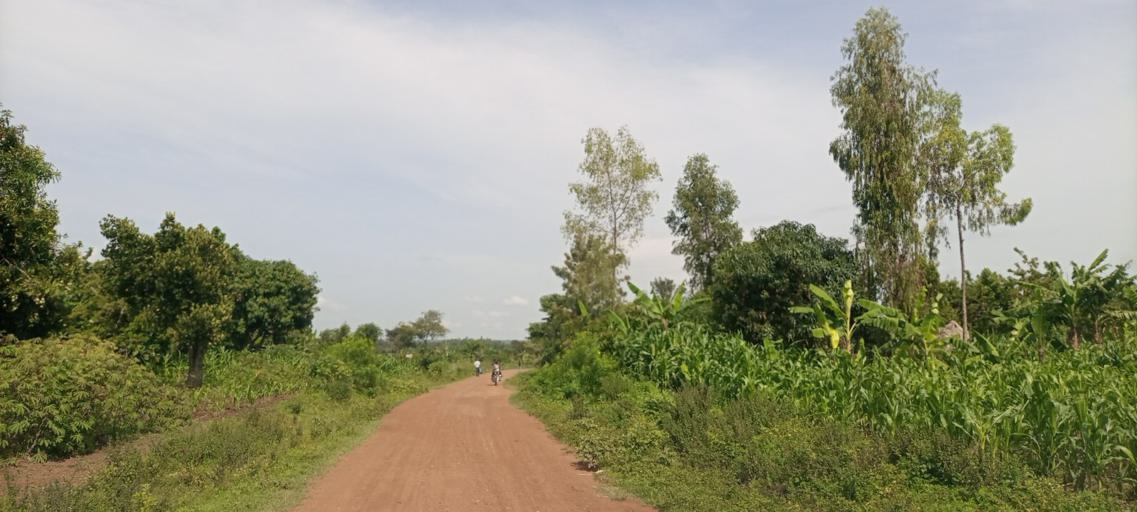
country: UG
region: Eastern Region
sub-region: Mbale District
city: Mbale
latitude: 1.1294
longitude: 34.0413
